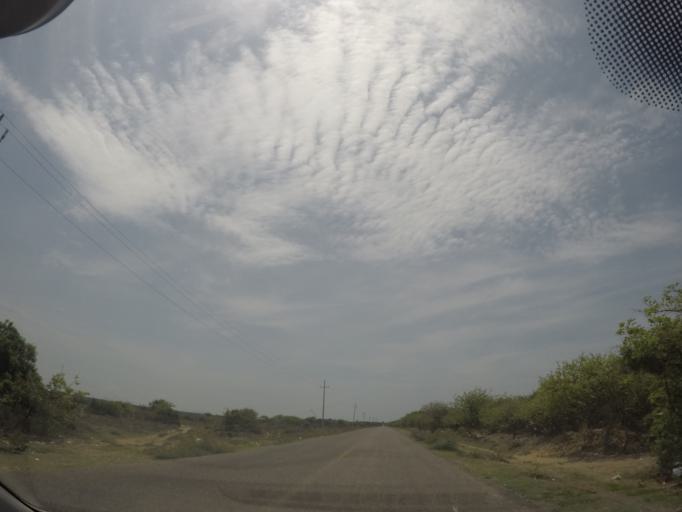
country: MX
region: Oaxaca
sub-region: San Mateo del Mar
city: Colonia Juarez
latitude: 16.2134
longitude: -95.0563
